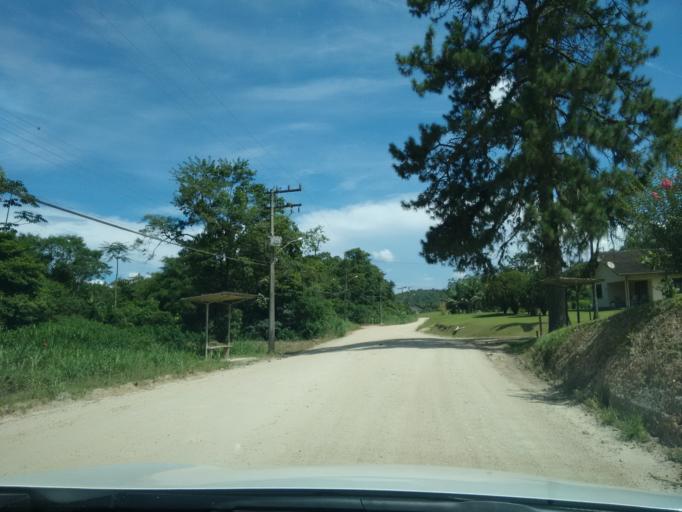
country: BR
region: Santa Catarina
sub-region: Pomerode
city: Pomerode
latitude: -26.6990
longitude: -49.1056
